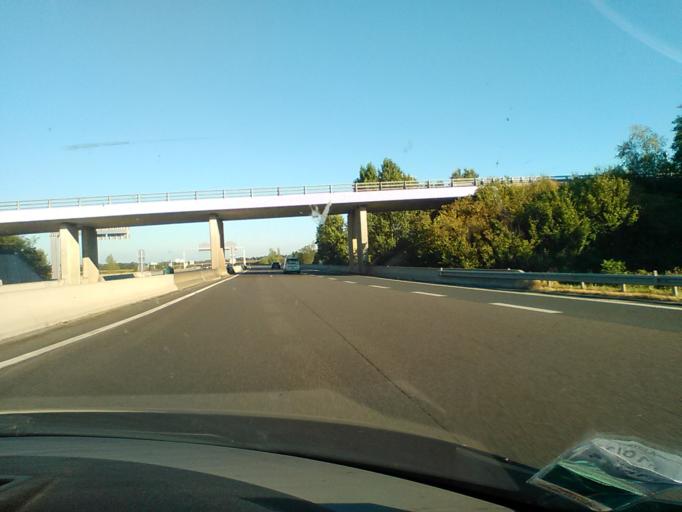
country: FR
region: Rhone-Alpes
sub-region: Departement de l'Ain
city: Thil
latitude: 45.8257
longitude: 5.0341
